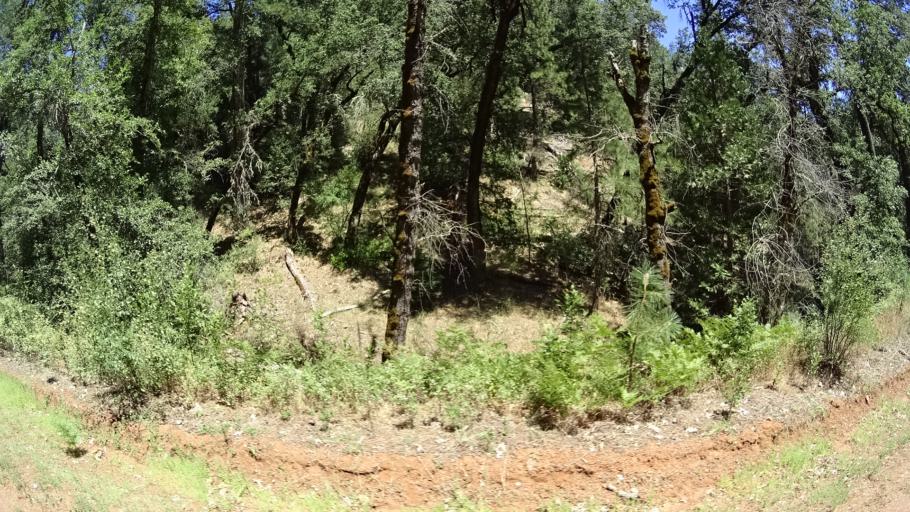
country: US
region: California
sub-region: Calaveras County
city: Mountain Ranch
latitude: 38.2974
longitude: -120.5039
